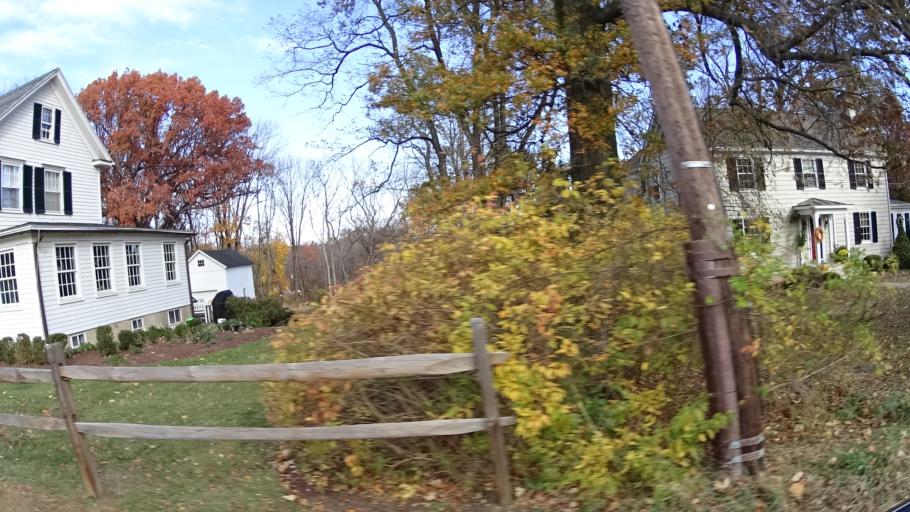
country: US
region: New Jersey
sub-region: Morris County
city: Madison
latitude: 40.7589
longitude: -74.4549
